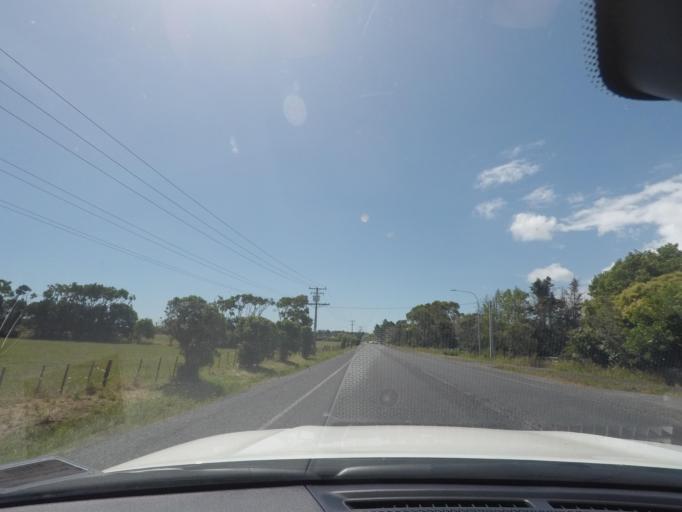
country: NZ
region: Auckland
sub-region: Auckland
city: Parakai
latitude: -36.6727
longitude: 174.4410
